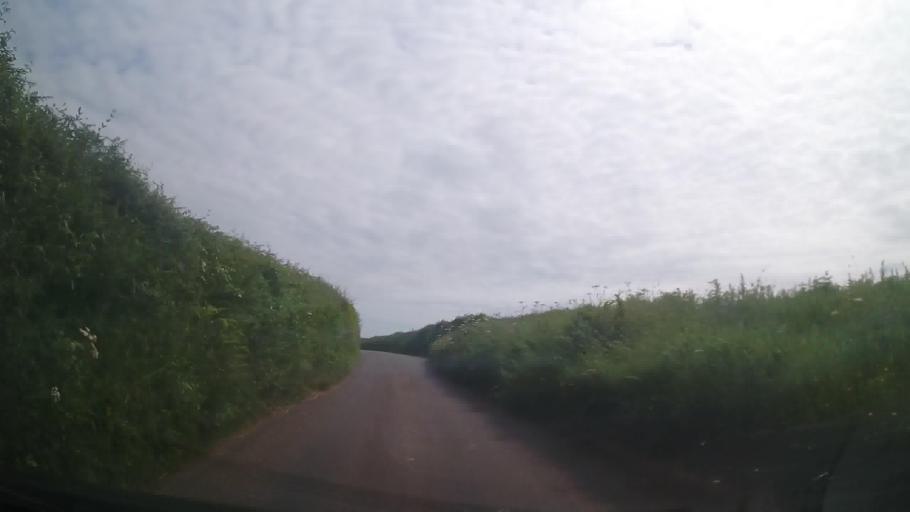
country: GB
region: England
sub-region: Devon
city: Salcombe
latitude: 50.2488
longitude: -3.6824
